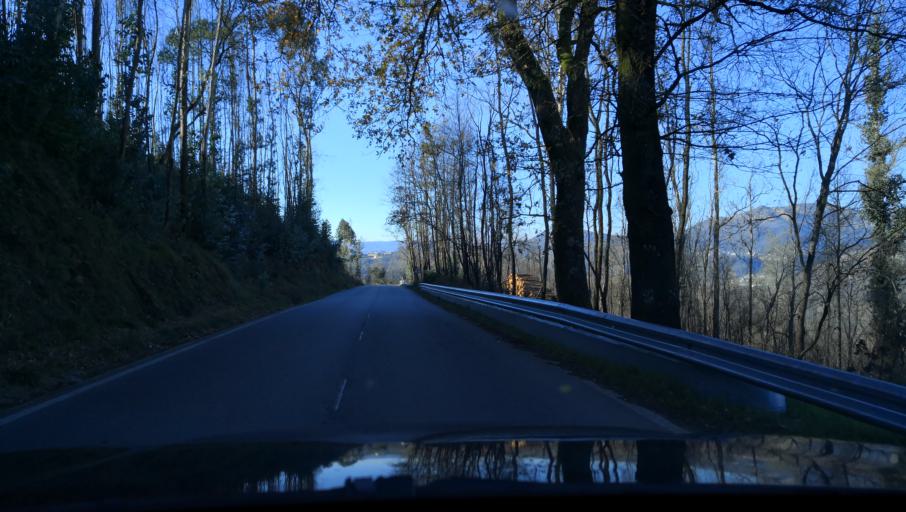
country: PT
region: Viseu
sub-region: Vouzela
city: Vouzela
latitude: 40.7303
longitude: -8.1417
